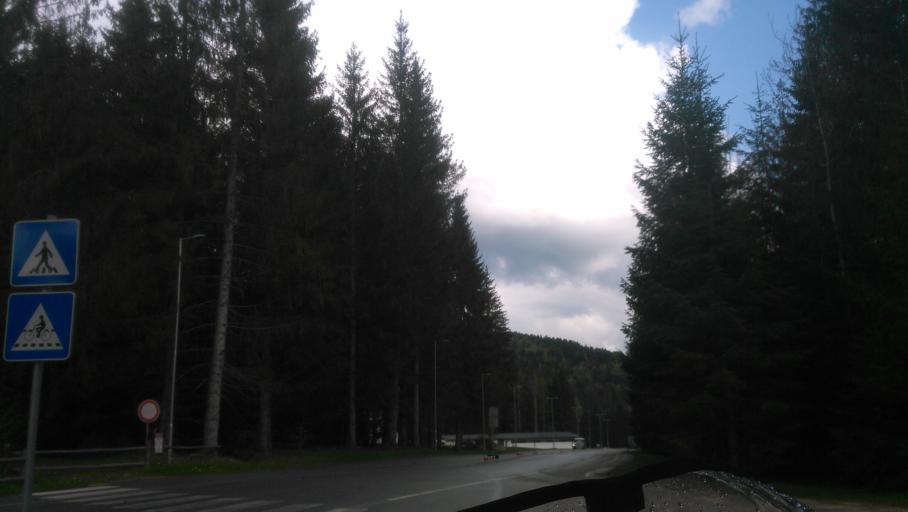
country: SK
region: Banskobystricky
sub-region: Okres Banska Bystrica
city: Brezno
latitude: 48.8658
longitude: 19.5980
